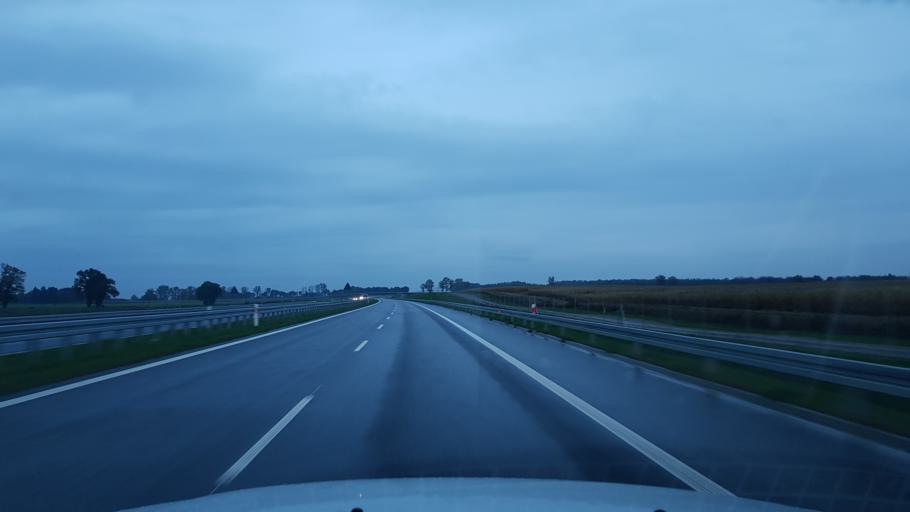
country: PL
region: West Pomeranian Voivodeship
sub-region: Powiat gryficki
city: Brojce
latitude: 53.8990
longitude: 15.3827
